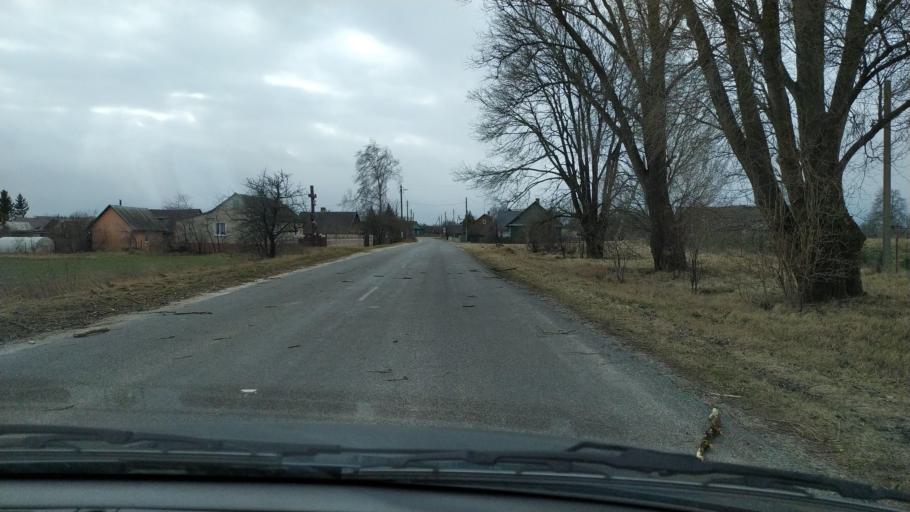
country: BY
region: Brest
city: Kamyanyets
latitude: 52.4093
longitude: 23.7978
